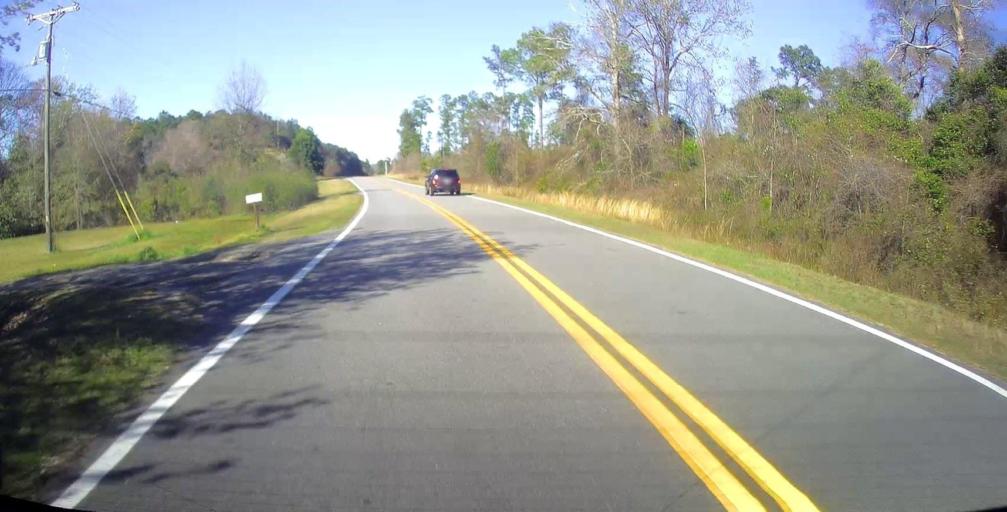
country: US
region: Georgia
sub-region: Peach County
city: Byron
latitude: 32.6791
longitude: -83.8087
